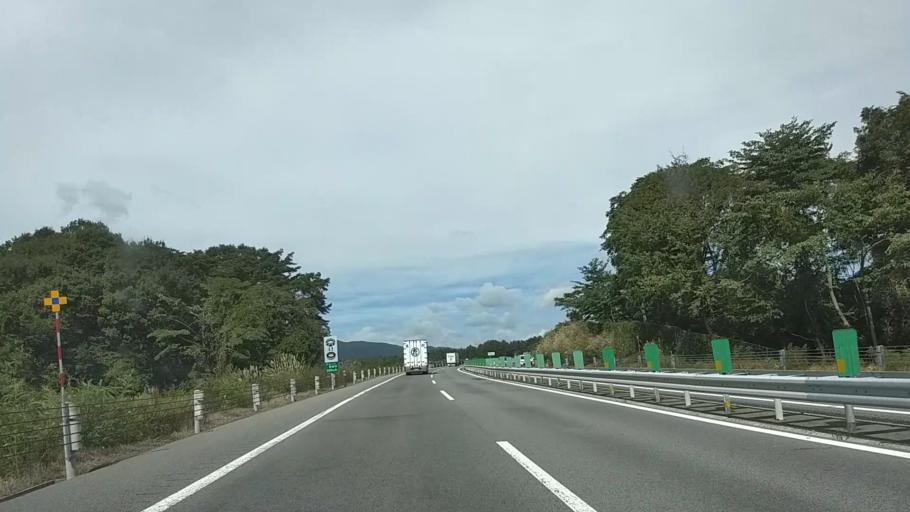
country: JP
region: Nagano
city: Chino
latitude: 35.9045
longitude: 138.2617
